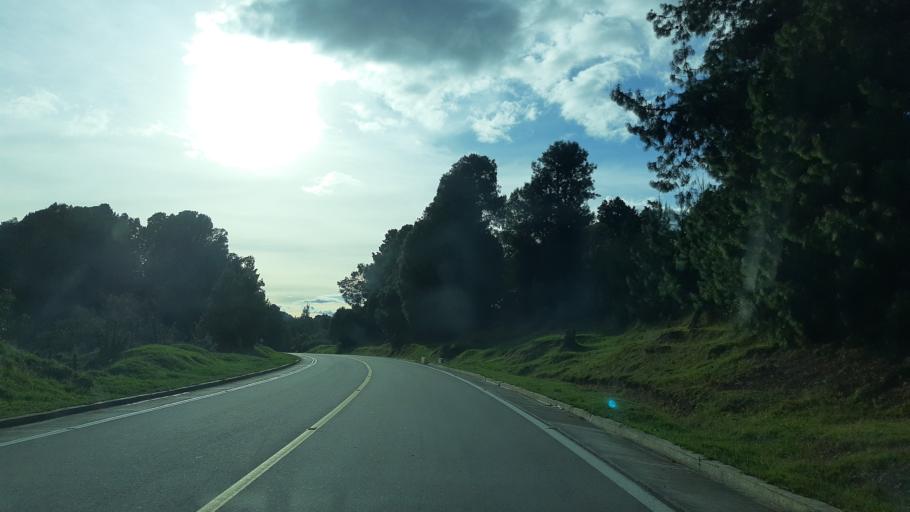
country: CO
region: Cundinamarca
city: Choconta
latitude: 5.0961
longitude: -73.7030
